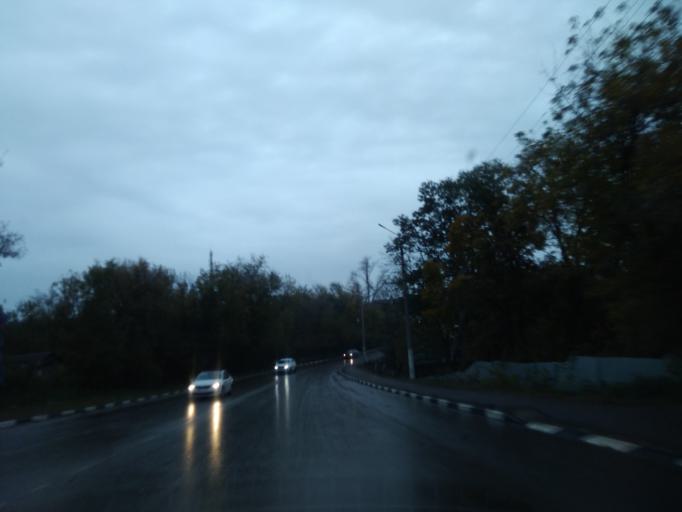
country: RU
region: Tula
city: Yefremov
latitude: 53.1361
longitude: 38.1159
